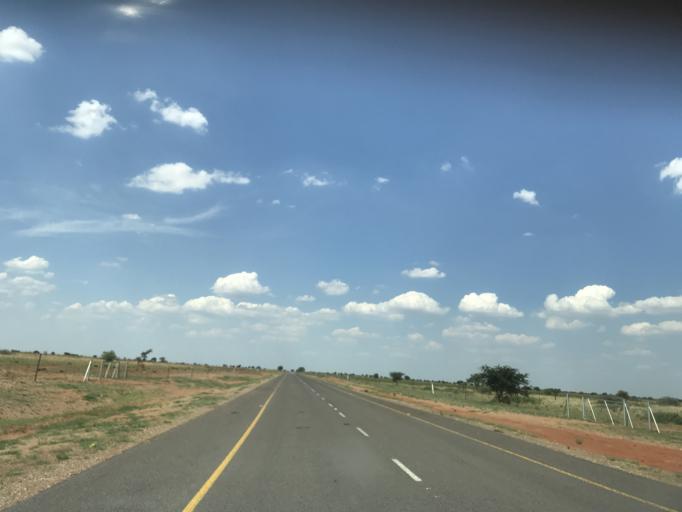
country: BW
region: South East
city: Janeng
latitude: -25.5390
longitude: 25.6149
